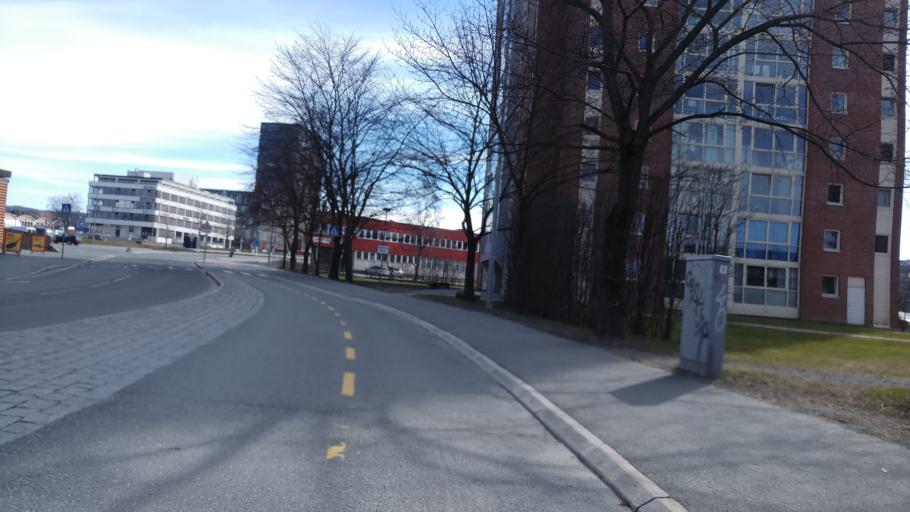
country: NO
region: Sor-Trondelag
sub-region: Trondheim
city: Trondheim
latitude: 63.4077
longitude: 10.3965
